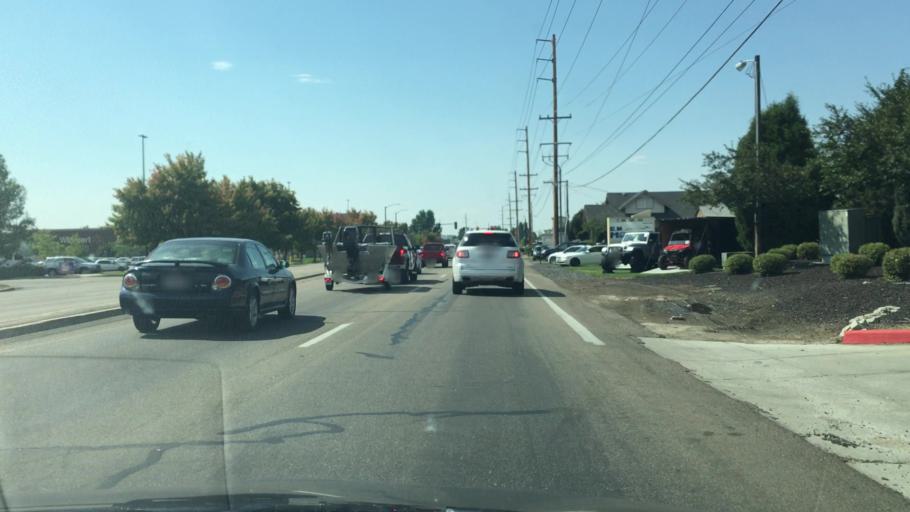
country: US
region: Idaho
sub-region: Ada County
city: Garden City
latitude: 43.6689
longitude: -116.2798
